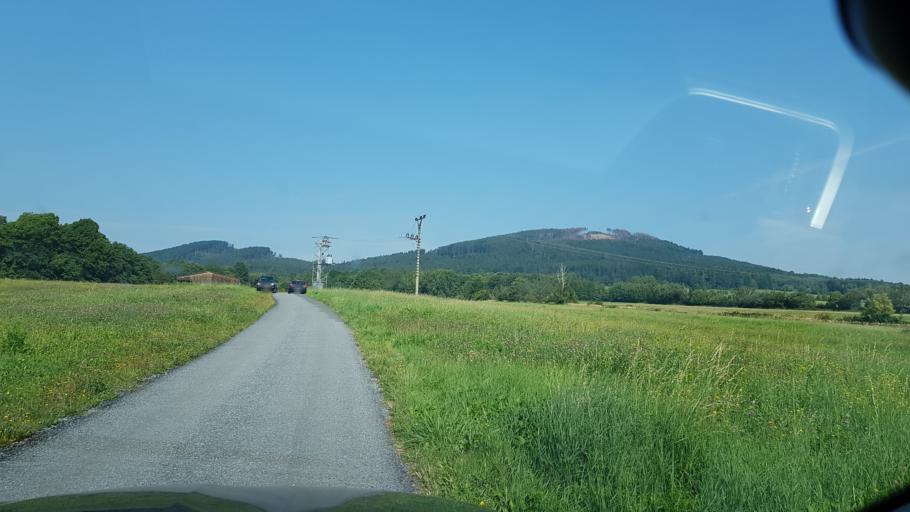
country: CZ
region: Olomoucky
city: Ceska Ves
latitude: 50.2672
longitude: 17.2380
